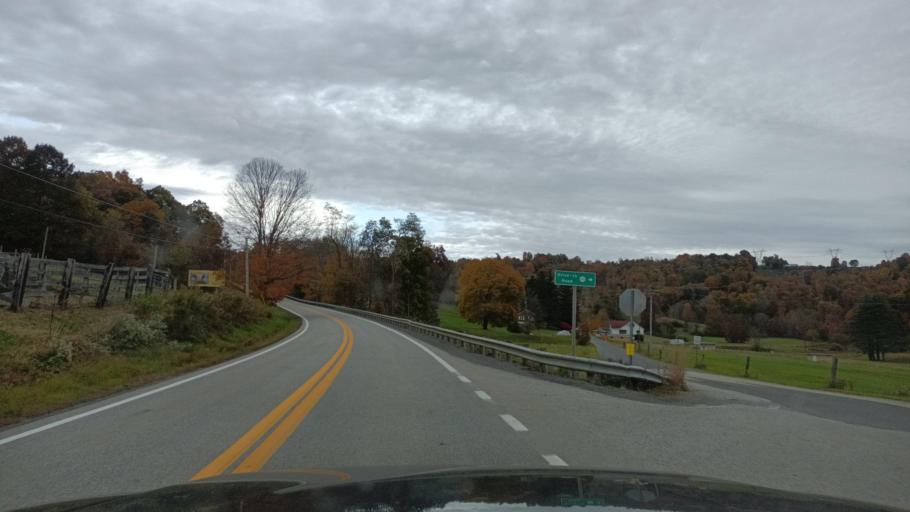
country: US
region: West Virginia
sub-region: Taylor County
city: Grafton
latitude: 39.3621
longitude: -79.9775
